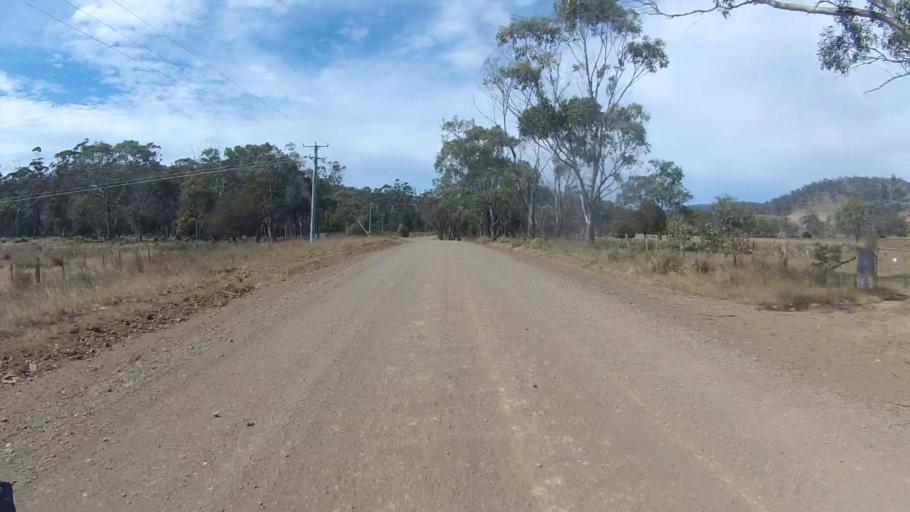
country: AU
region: Tasmania
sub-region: Sorell
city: Sorell
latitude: -42.6465
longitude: 147.8997
